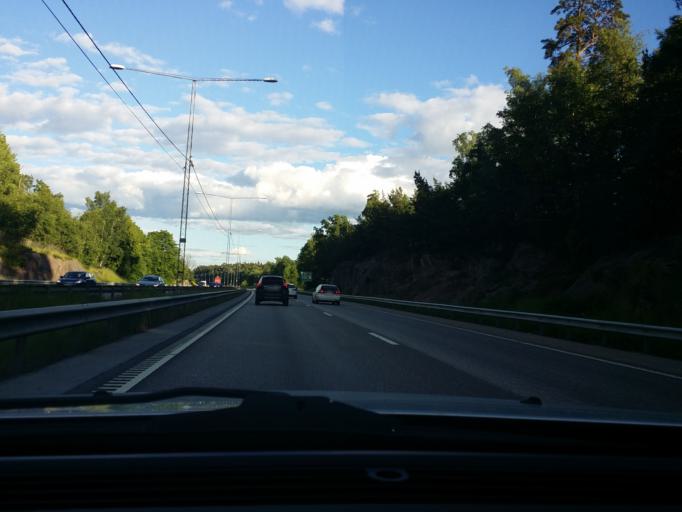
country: SE
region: Stockholm
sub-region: Upplands Vasby Kommun
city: Upplands Vaesby
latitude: 59.5402
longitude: 17.9065
